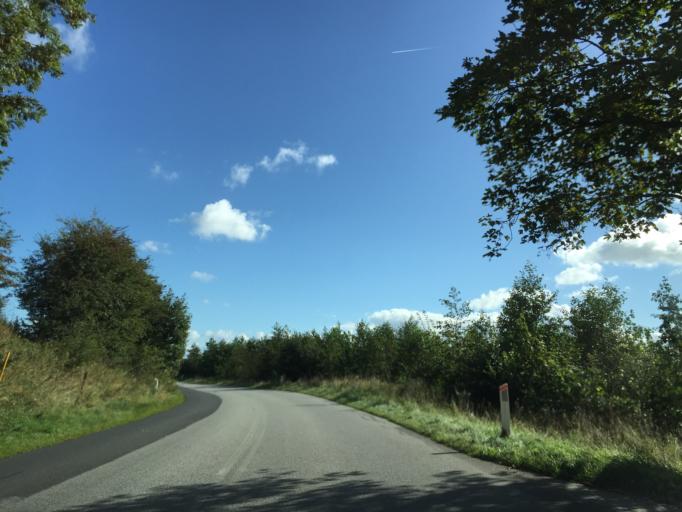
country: DK
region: Central Jutland
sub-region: Viborg Kommune
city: Viborg
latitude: 56.4400
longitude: 9.5075
